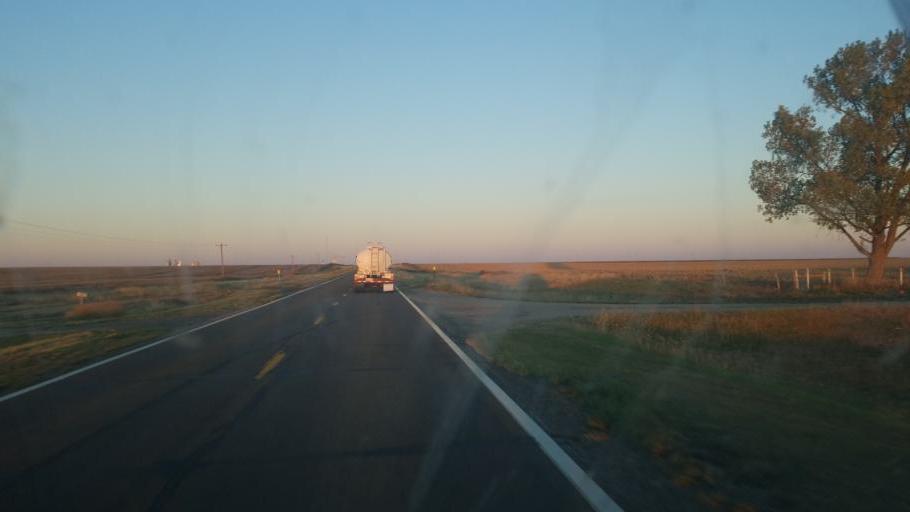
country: US
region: Kansas
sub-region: Wallace County
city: Sharon Springs
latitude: 38.9021
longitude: -101.7125
